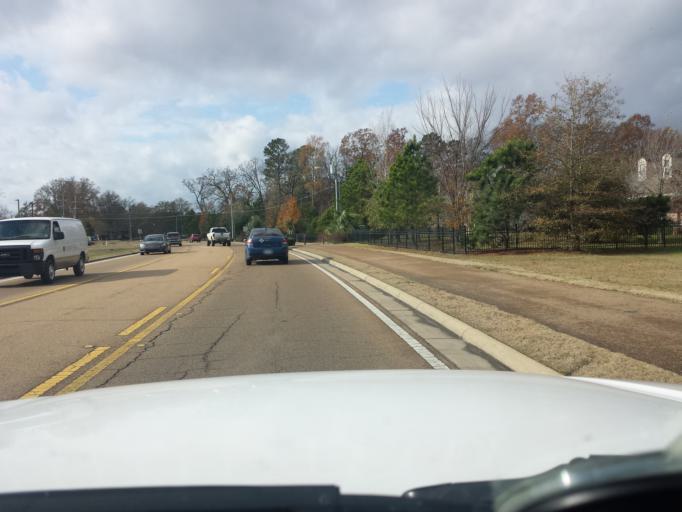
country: US
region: Mississippi
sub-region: Rankin County
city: Flowood
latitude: 32.3433
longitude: -90.0712
